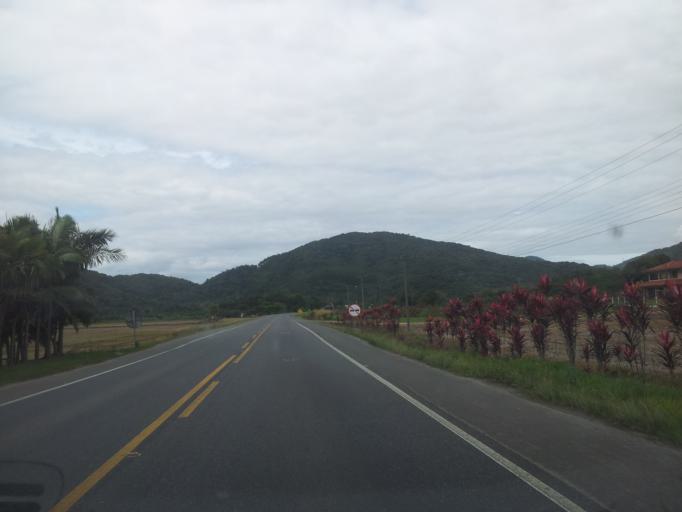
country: BR
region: Santa Catarina
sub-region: Guaramirim
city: Guaramirim
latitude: -26.3886
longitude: -48.9510
